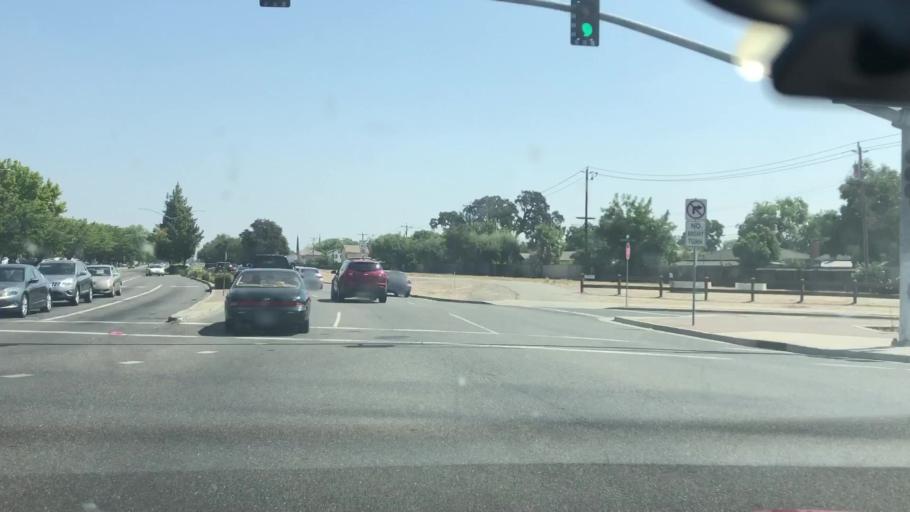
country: US
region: California
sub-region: San Joaquin County
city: Lincoln Village
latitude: 37.9913
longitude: -121.3126
